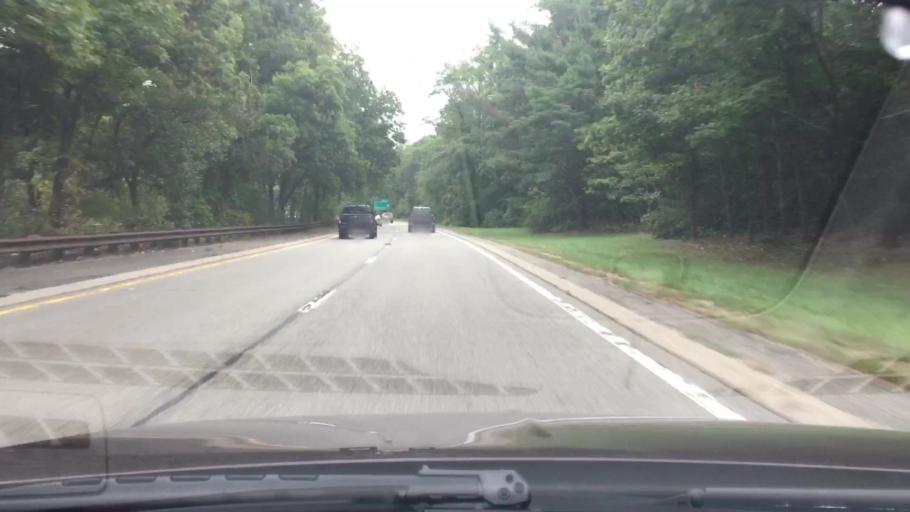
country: US
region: New York
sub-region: Suffolk County
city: Commack
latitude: 40.8203
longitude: -73.3030
